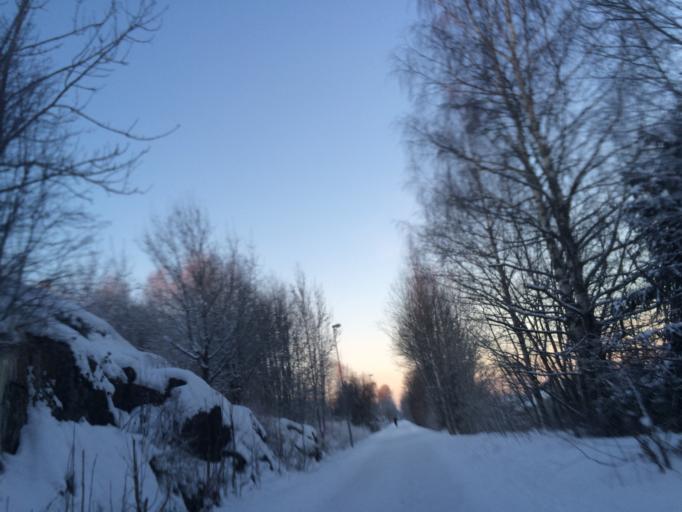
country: NO
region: Akershus
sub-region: Ski
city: Ski
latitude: 59.7068
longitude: 10.8348
